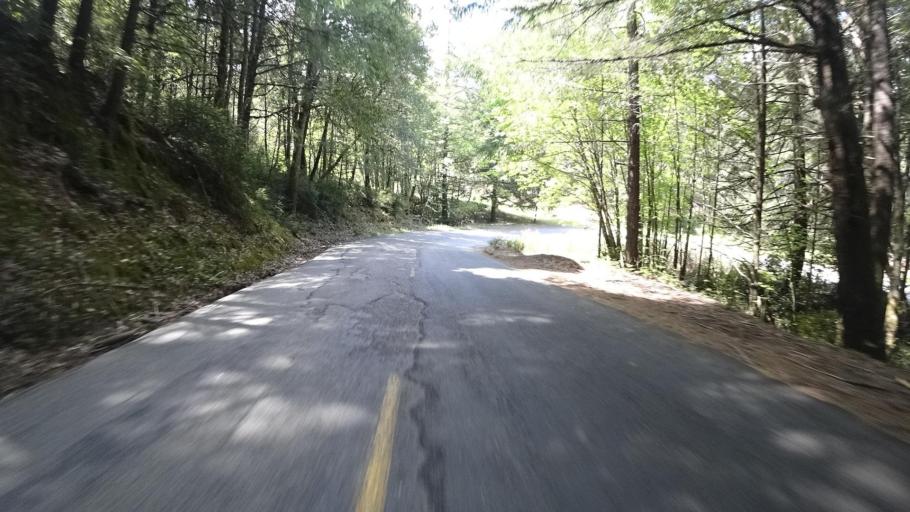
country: US
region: California
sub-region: Humboldt County
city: Redway
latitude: 40.0913
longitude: -123.9383
